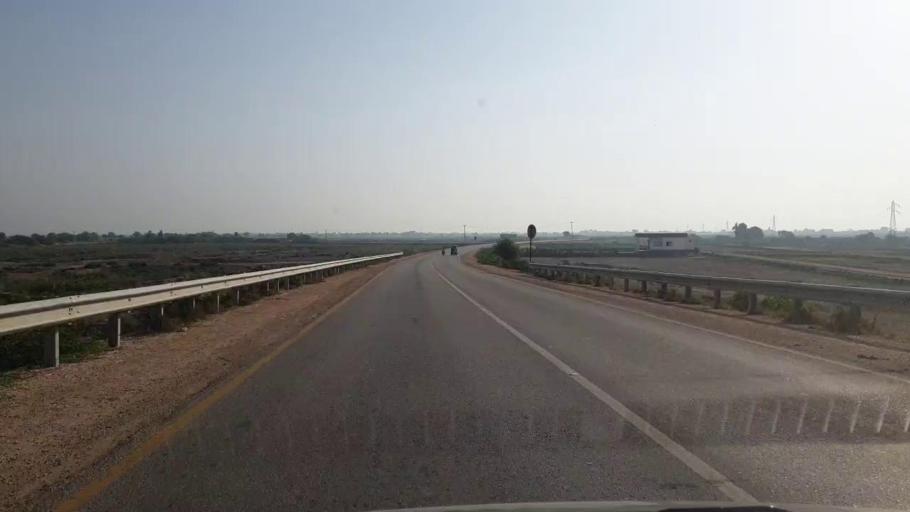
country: PK
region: Sindh
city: Badin
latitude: 24.6810
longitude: 68.8350
